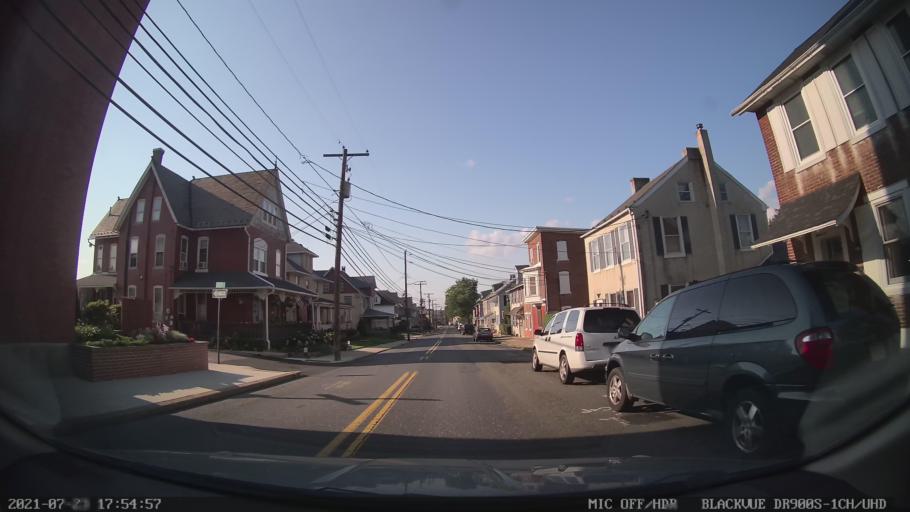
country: US
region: Pennsylvania
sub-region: Lehigh County
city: Macungie
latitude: 40.5130
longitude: -75.5554
